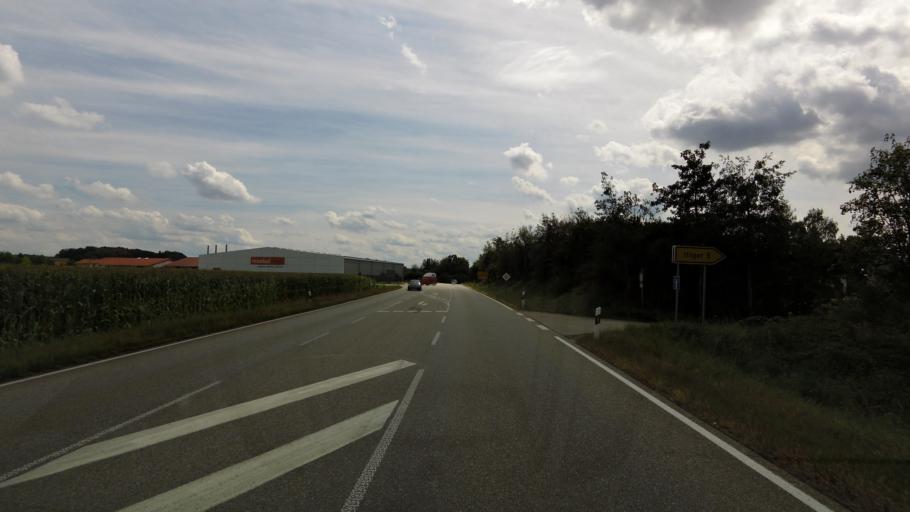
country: DE
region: Bavaria
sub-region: Upper Bavaria
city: Unterneukirchen
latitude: 48.1569
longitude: 12.6113
